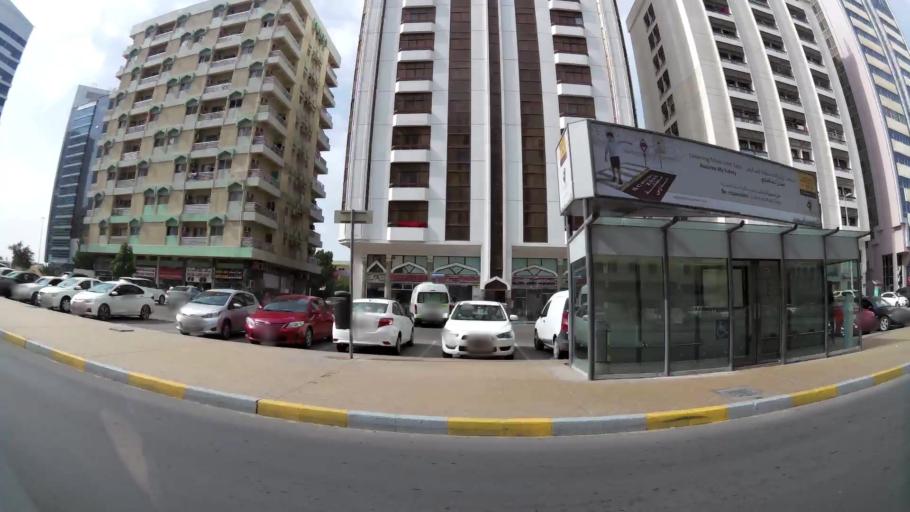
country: AE
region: Abu Dhabi
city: Abu Dhabi
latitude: 24.4612
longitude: 54.3789
